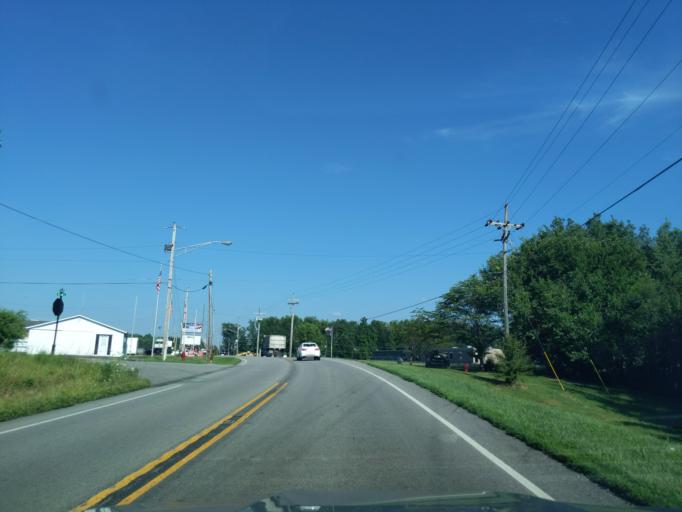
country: US
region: Indiana
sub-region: Ripley County
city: Versailles
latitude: 39.0712
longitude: -85.2678
